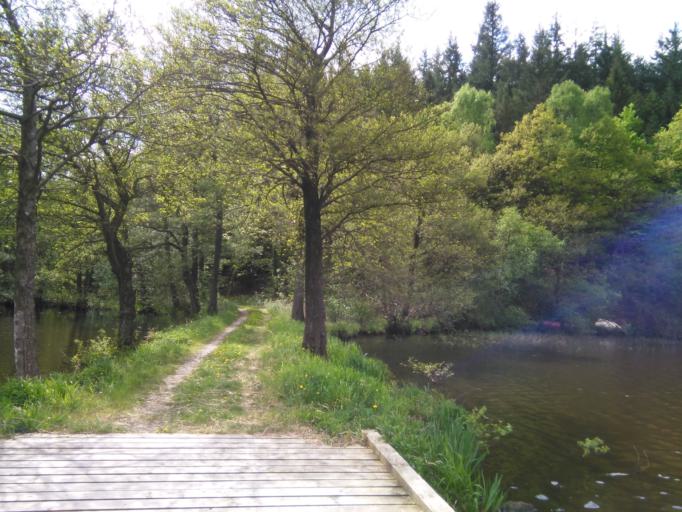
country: DK
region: Central Jutland
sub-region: Silkeborg Kommune
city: Svejbaek
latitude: 56.0621
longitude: 9.6025
